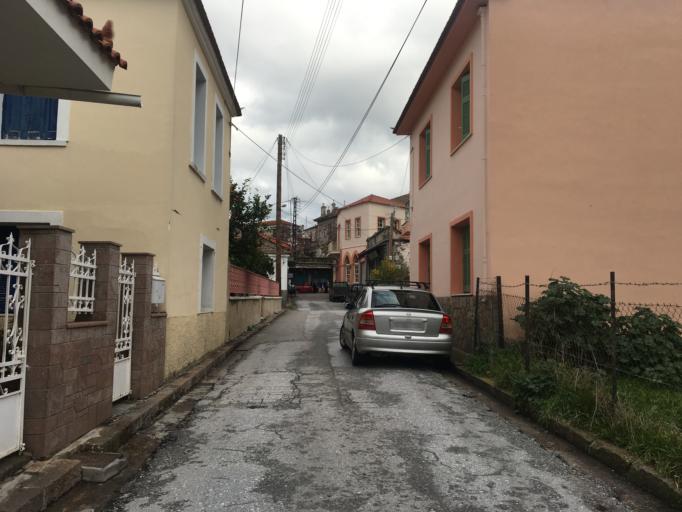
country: GR
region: North Aegean
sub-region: Nomos Lesvou
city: Agia Paraskevi
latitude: 39.2479
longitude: 26.2702
